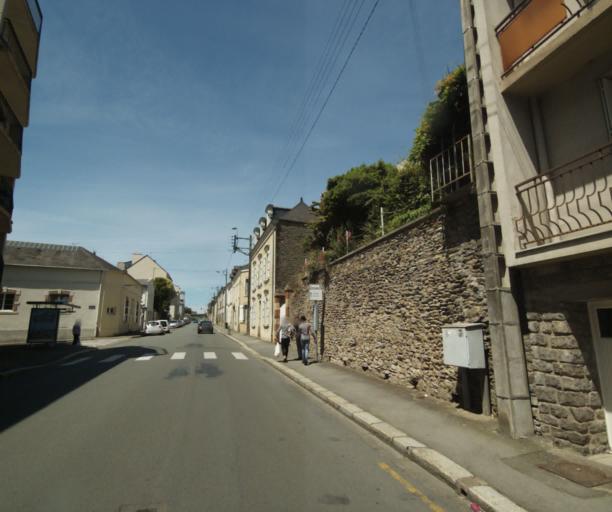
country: FR
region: Pays de la Loire
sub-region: Departement de la Mayenne
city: Laval
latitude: 48.0742
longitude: -0.7821
